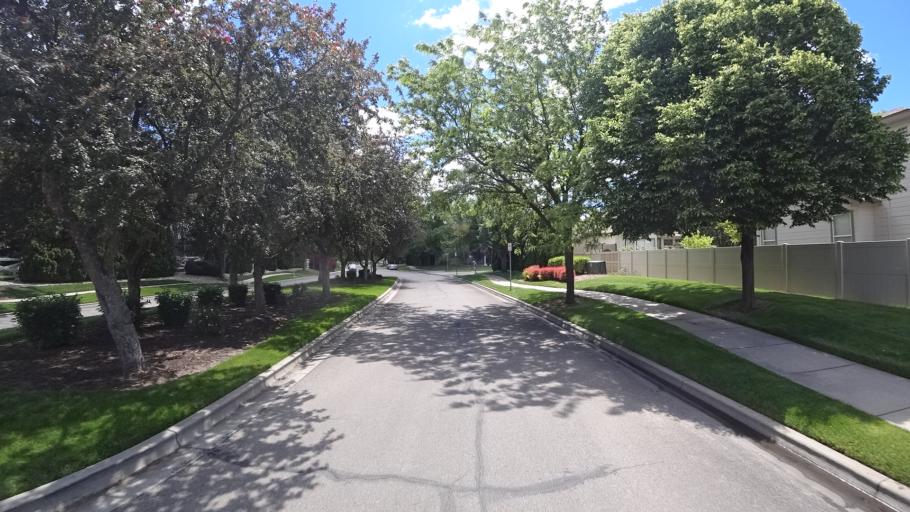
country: US
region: Idaho
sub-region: Ada County
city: Eagle
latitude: 43.6617
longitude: -116.3468
